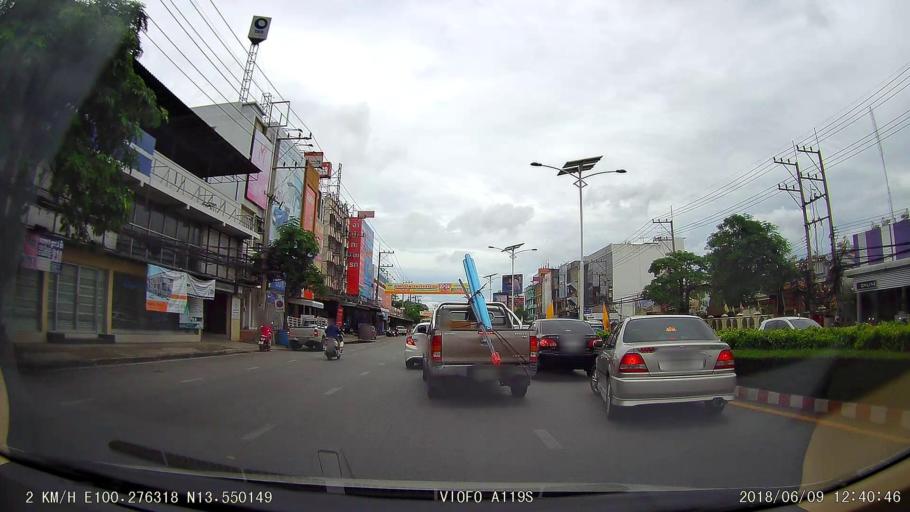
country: TH
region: Samut Sakhon
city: Samut Sakhon
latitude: 13.5501
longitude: 100.2763
